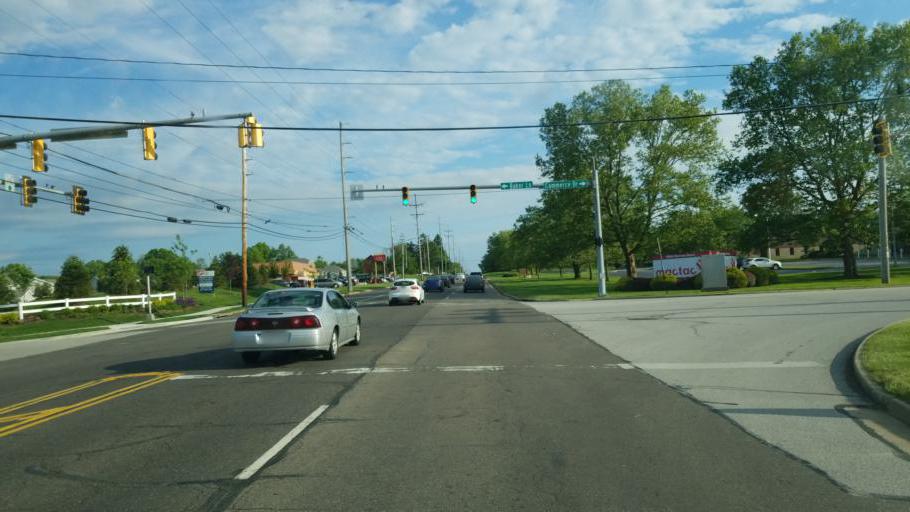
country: US
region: Ohio
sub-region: Summit County
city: Stow
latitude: 41.1911
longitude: -81.4405
